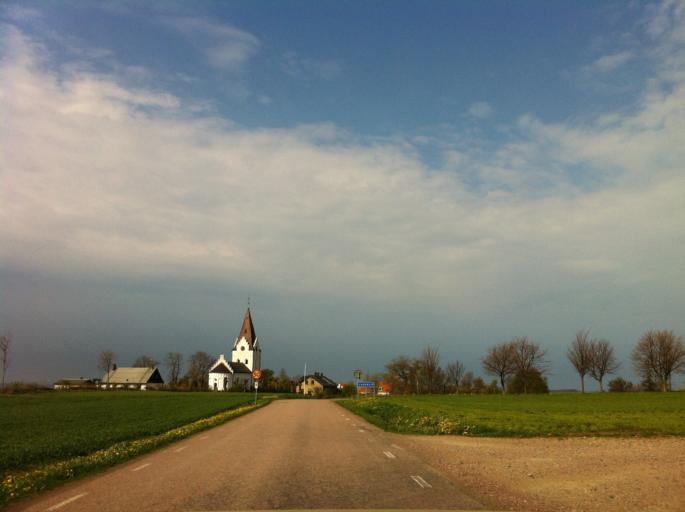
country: SE
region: Skane
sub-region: Landskrona
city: Asmundtorp
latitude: 55.9044
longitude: 12.9049
